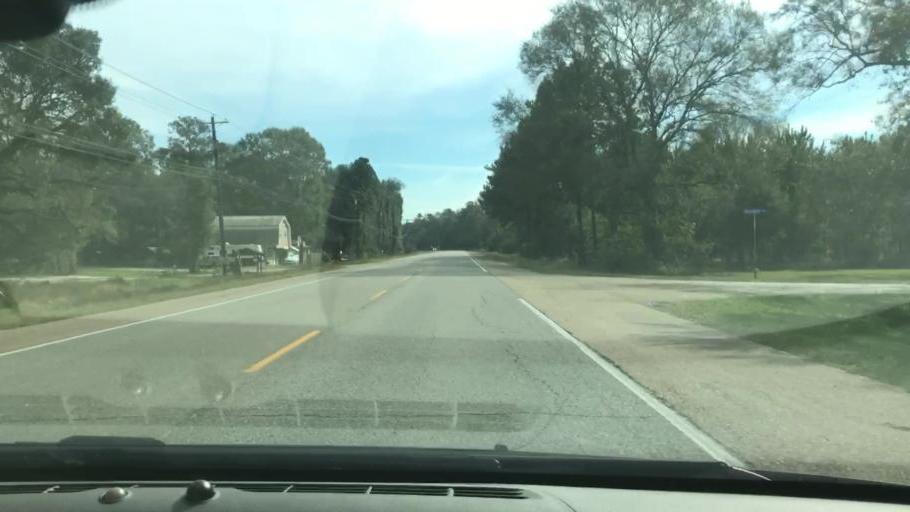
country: US
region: Louisiana
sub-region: Saint Tammany Parish
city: Pearl River
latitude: 30.4093
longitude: -89.7758
